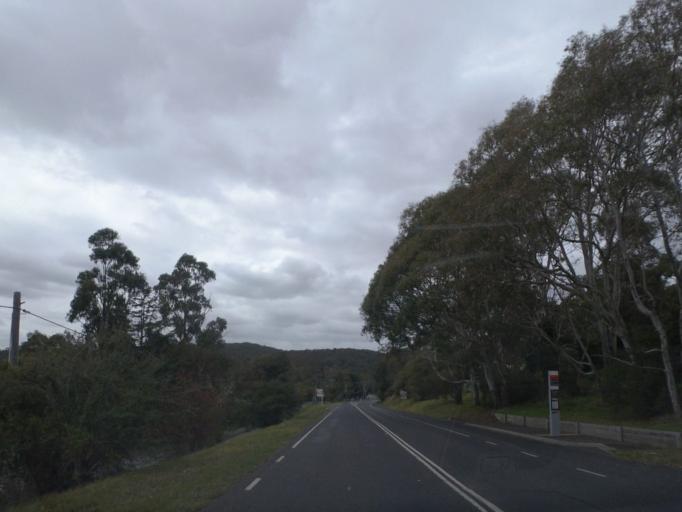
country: AU
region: Victoria
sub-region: Nillumbik
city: North Warrandyte
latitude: -37.7452
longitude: 145.2038
